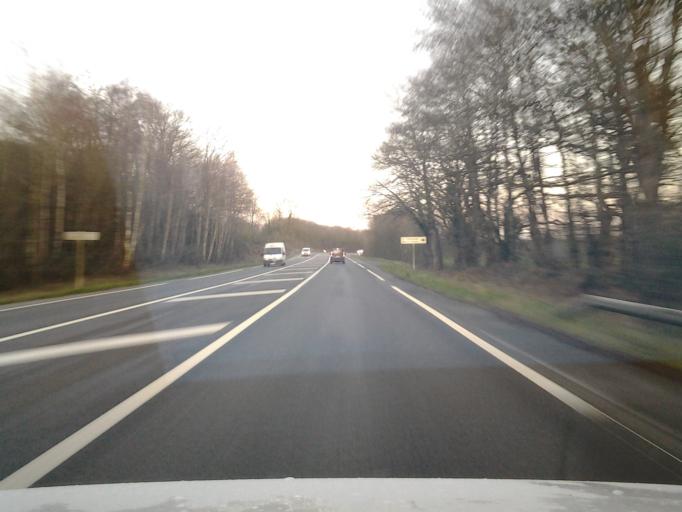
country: FR
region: Pays de la Loire
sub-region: Departement de la Vendee
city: Les Epesses
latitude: 46.8900
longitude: -0.9182
